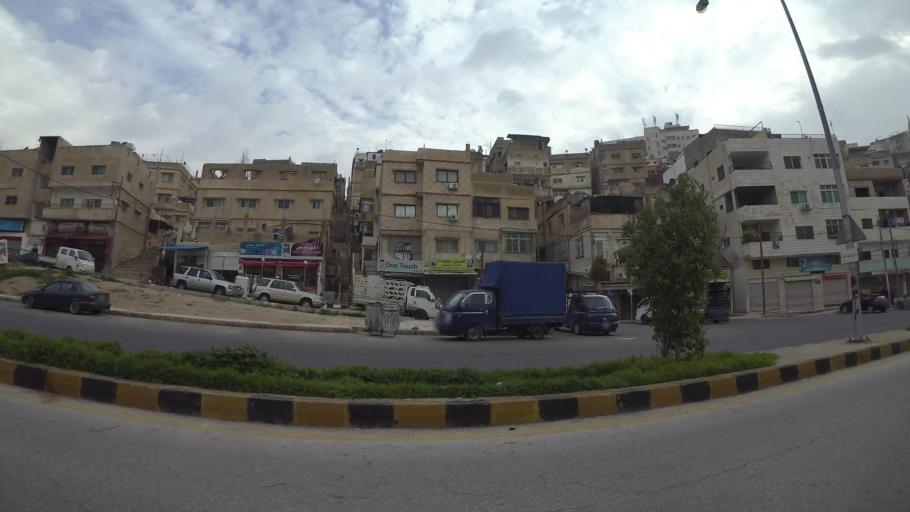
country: JO
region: Amman
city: Amman
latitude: 31.9645
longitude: 35.9343
